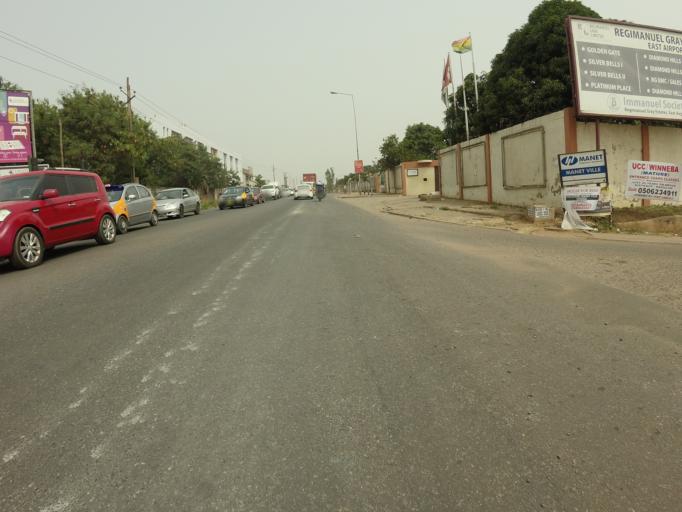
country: GH
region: Greater Accra
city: Medina Estates
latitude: 5.6348
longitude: -0.1334
